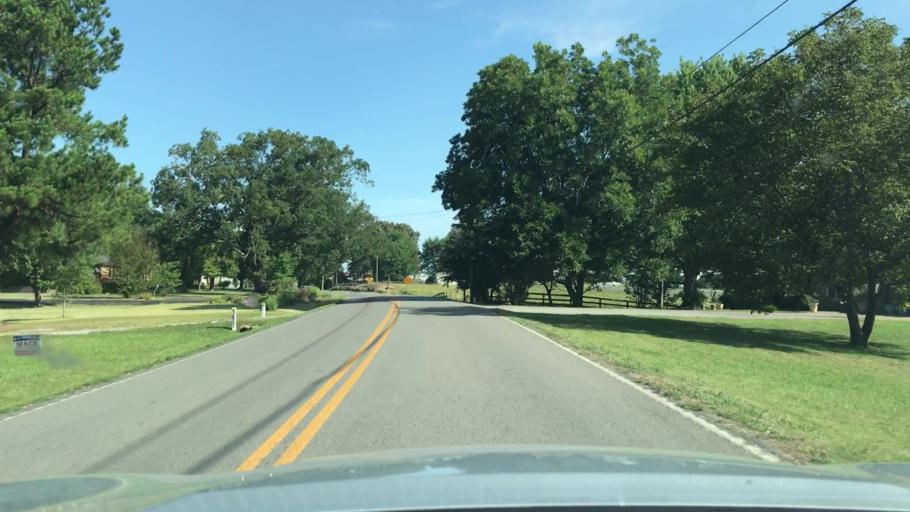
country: US
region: Kentucky
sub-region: Muhlenberg County
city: Greenville
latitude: 37.1613
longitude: -87.1426
